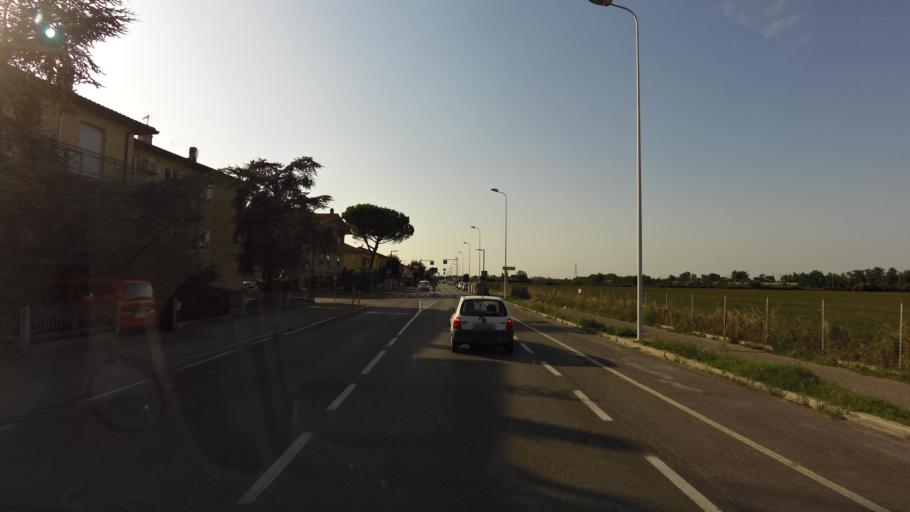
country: IT
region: Emilia-Romagna
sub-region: Provincia di Ravenna
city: Classe
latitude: 44.3904
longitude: 12.2215
